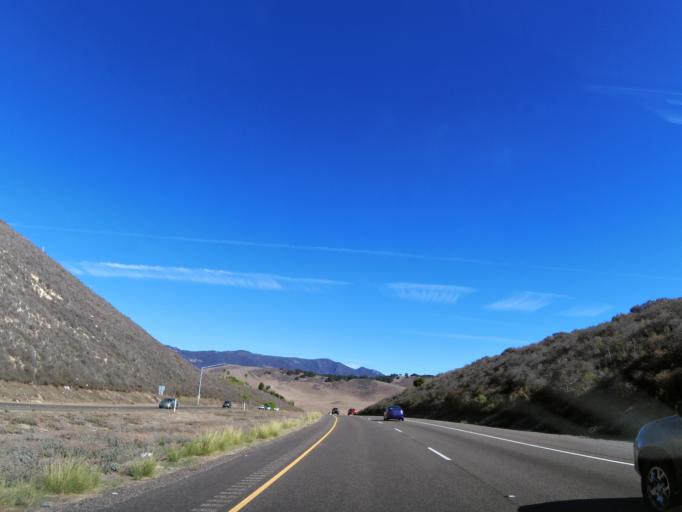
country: US
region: California
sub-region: Santa Barbara County
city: Solvang
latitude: 34.4626
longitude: -120.0767
